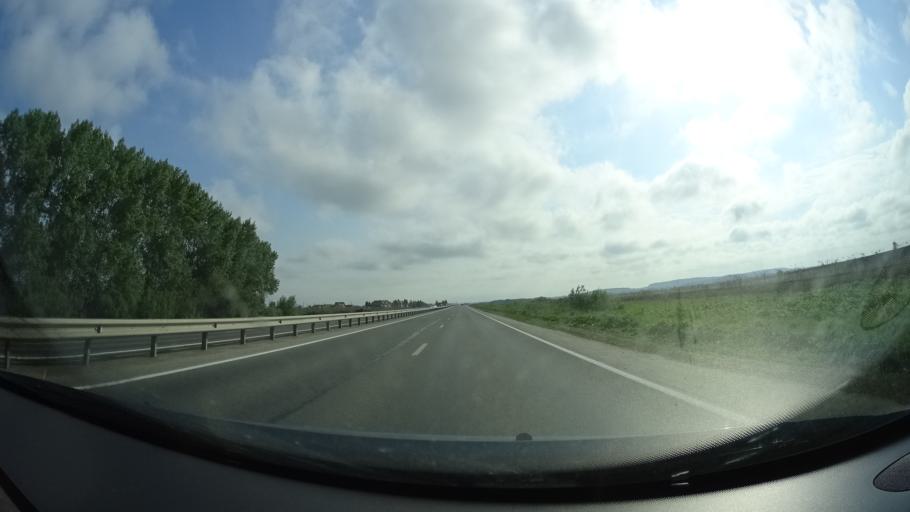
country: RU
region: Perm
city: Kultayevo
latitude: 57.8900
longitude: 55.9484
